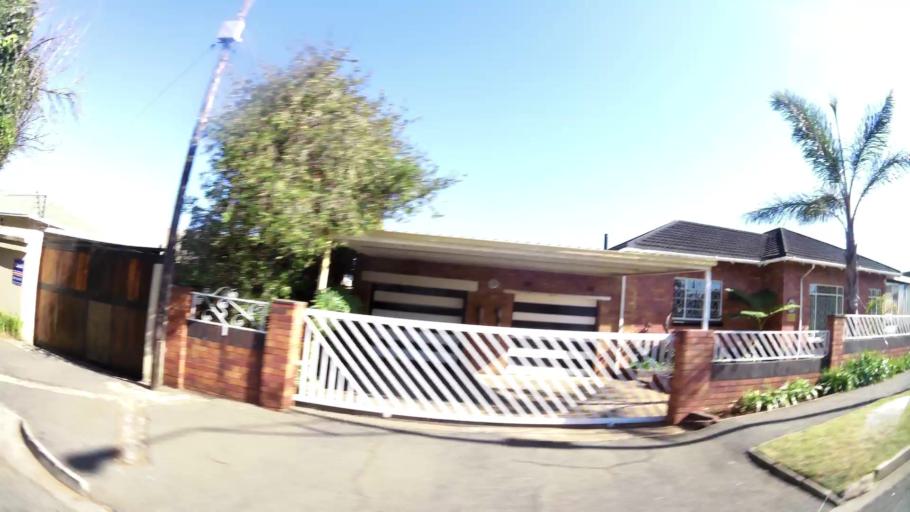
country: ZA
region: Gauteng
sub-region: City of Johannesburg Metropolitan Municipality
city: Johannesburg
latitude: -26.1946
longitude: 27.9915
